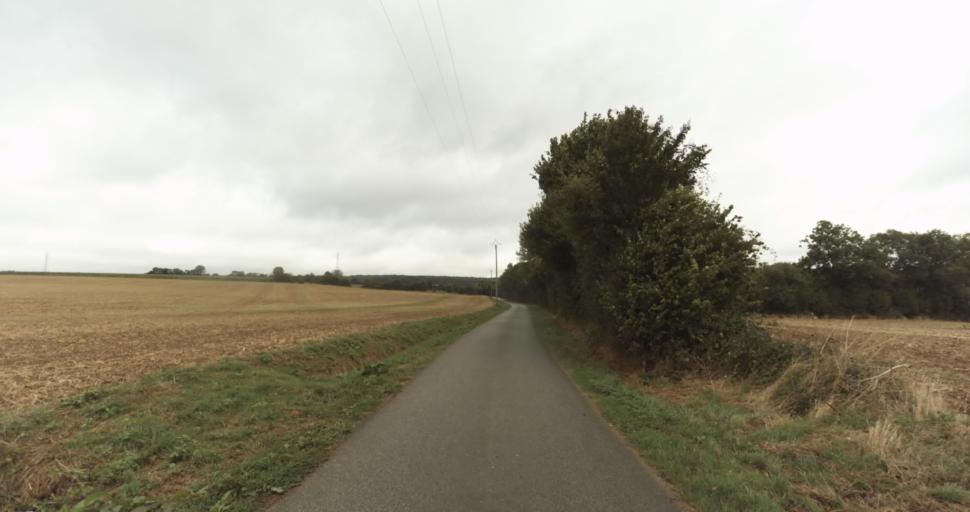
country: FR
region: Lower Normandy
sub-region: Departement de l'Orne
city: Sainte-Gauburge-Sainte-Colombe
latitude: 48.7404
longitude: 0.4538
